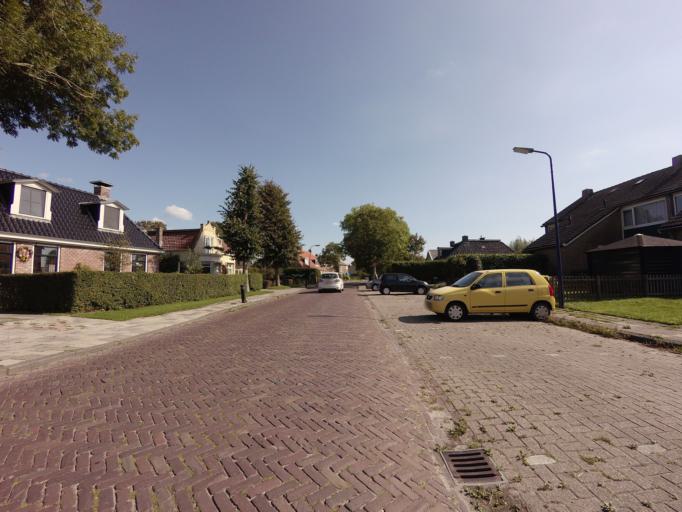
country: NL
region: Friesland
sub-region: Gemeente Littenseradiel
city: Makkum
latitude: 53.1004
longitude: 5.6453
